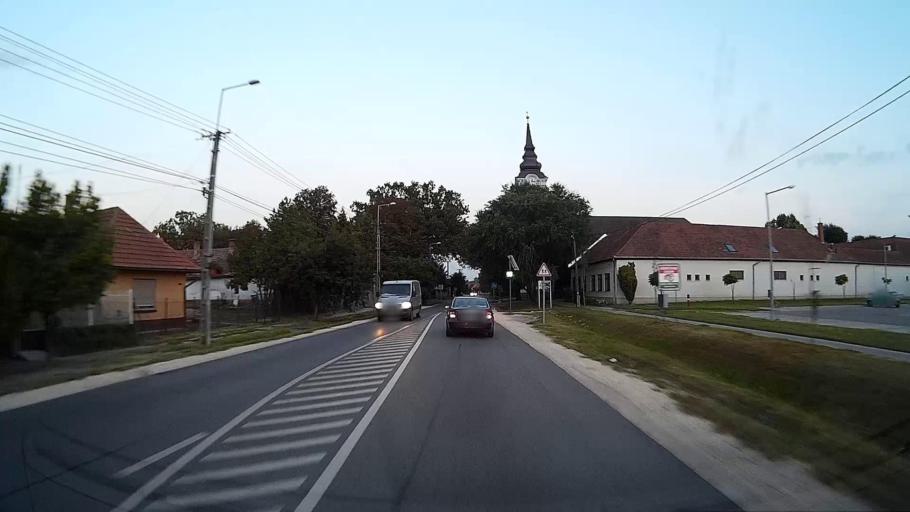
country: HU
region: Pest
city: Albertirsa
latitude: 47.2525
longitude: 19.6044
